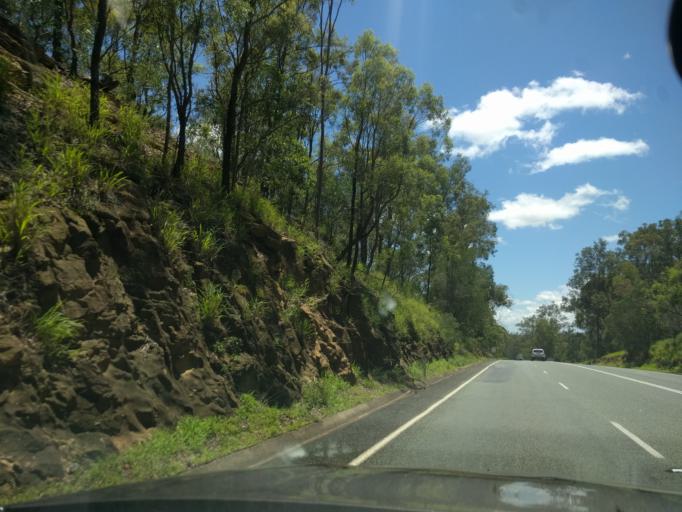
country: AU
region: Queensland
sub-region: Logan
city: Cedar Vale
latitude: -27.8530
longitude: 153.0123
